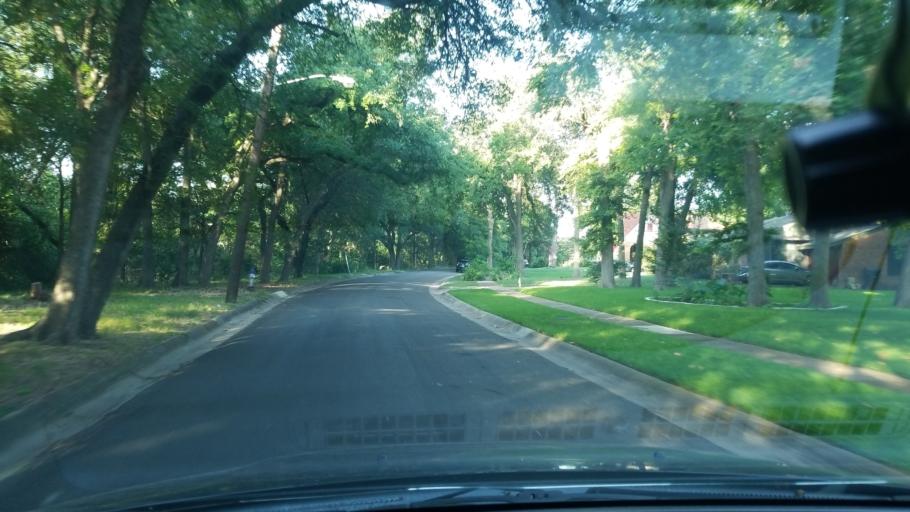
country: US
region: Texas
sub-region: Dallas County
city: Dallas
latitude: 32.7331
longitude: -96.8208
